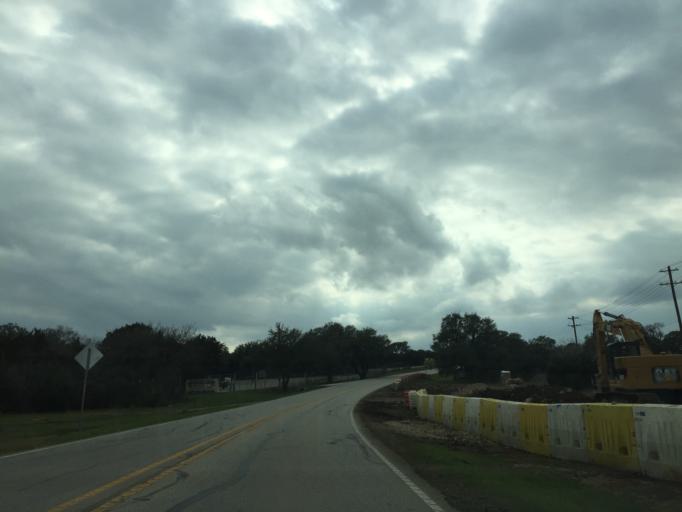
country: US
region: Texas
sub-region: Travis County
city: Shady Hollow
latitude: 30.1592
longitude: -97.9557
